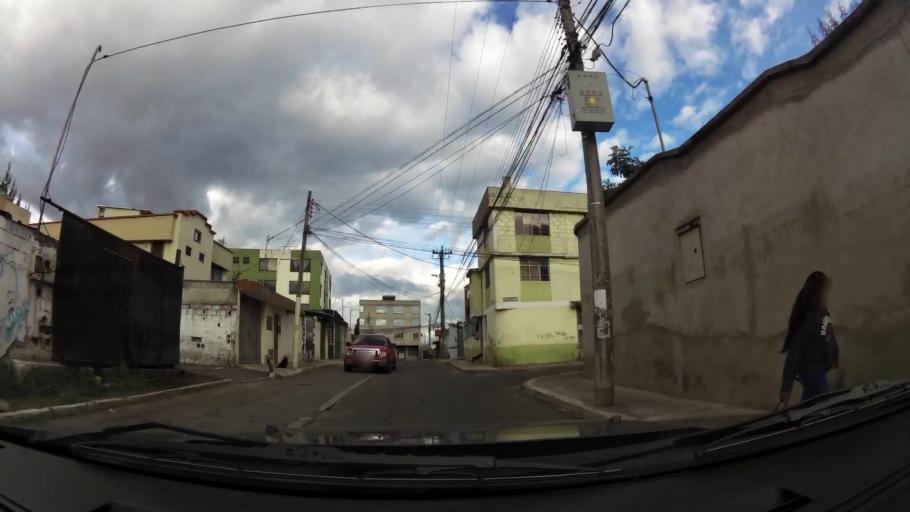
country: EC
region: Pichincha
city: Quito
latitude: -0.1337
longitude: -78.4639
